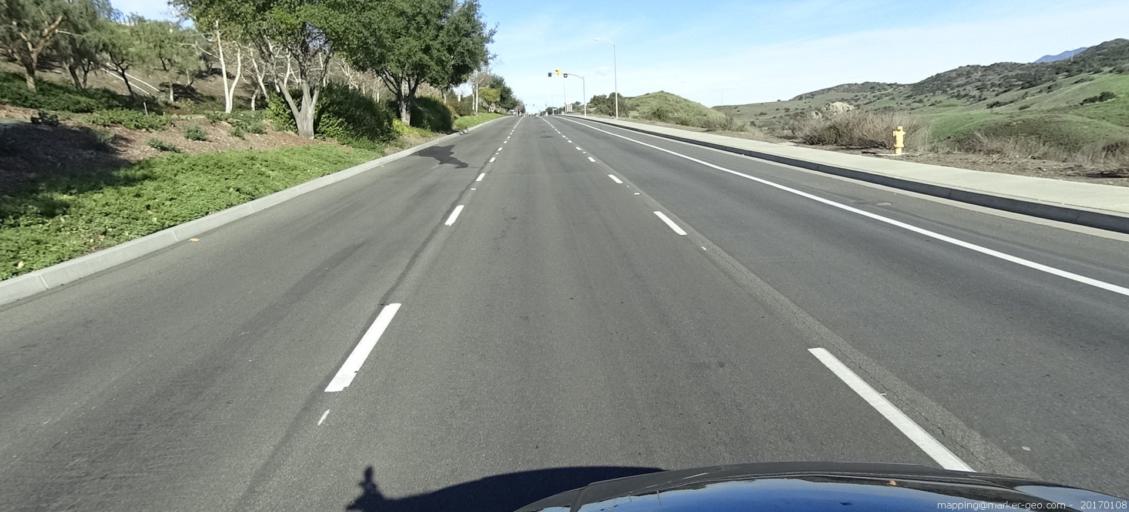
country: US
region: California
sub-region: Orange County
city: Ladera Ranch
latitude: 33.5366
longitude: -117.6249
